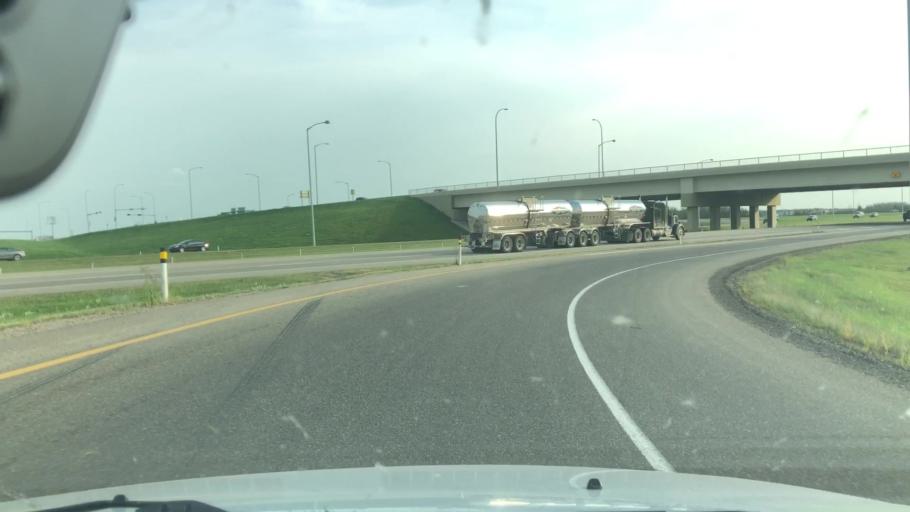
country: CA
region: Alberta
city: St. Albert
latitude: 53.6402
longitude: -113.5445
